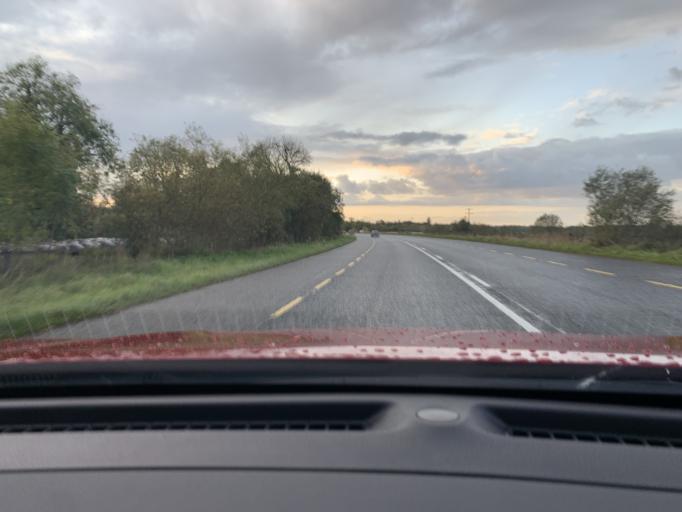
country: IE
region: Connaught
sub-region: County Leitrim
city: Carrick-on-Shannon
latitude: 53.9479
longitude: -8.1241
